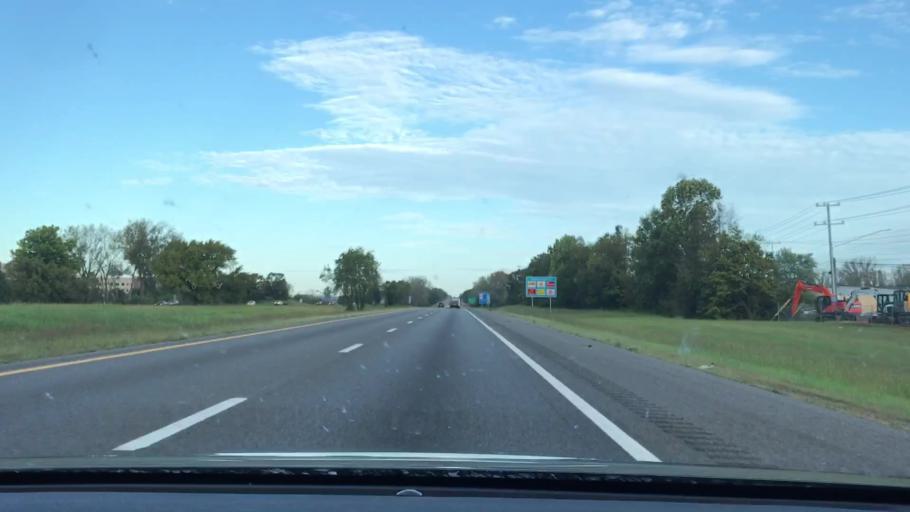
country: US
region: Tennessee
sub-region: Montgomery County
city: Clarksville
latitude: 36.5796
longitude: -87.2642
